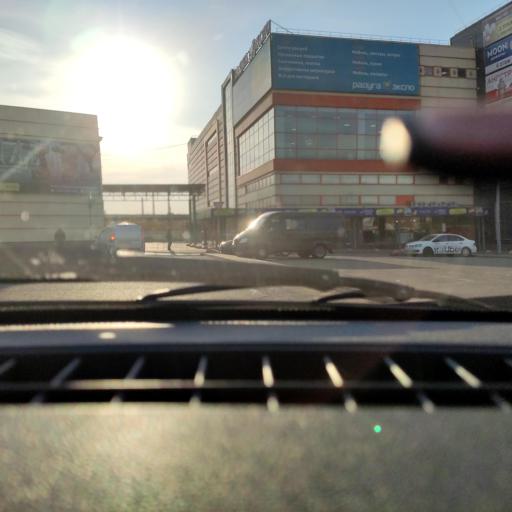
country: RU
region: Bashkortostan
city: Ufa
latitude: 54.8022
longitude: 56.0945
